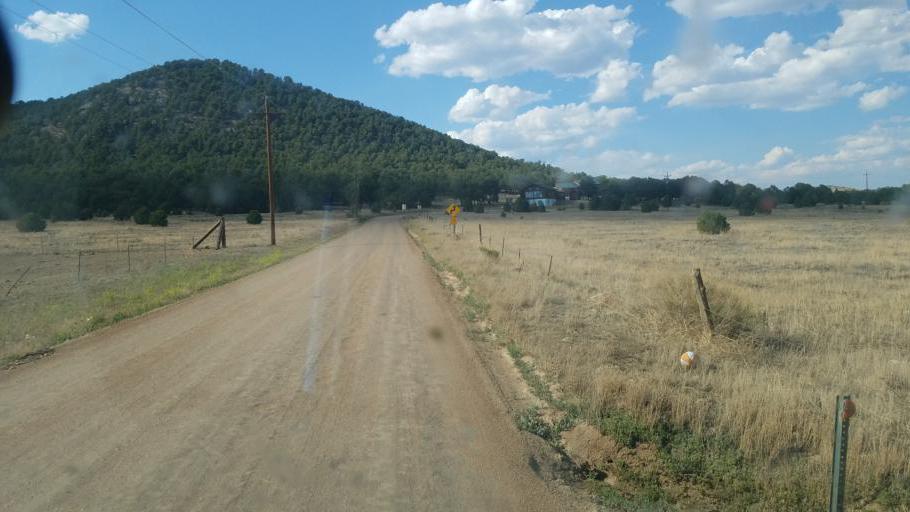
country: US
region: Colorado
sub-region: Custer County
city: Westcliffe
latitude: 38.2961
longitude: -105.4911
